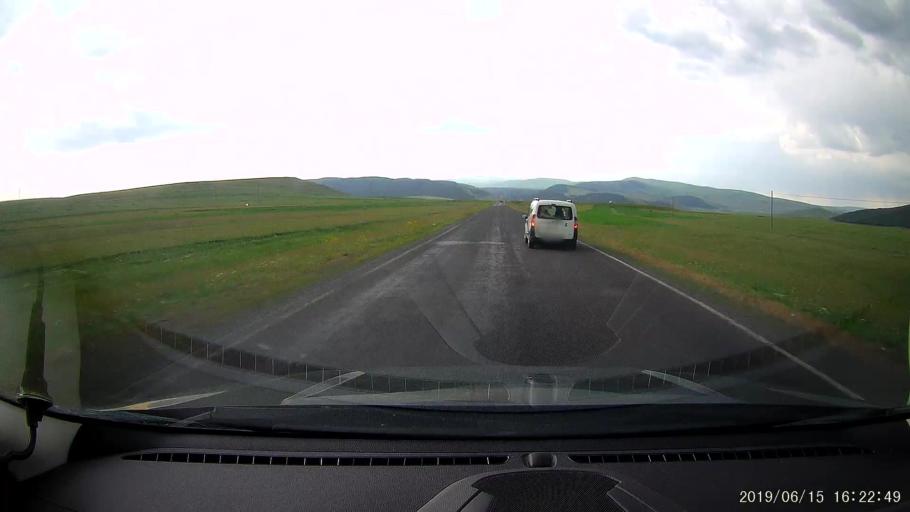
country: TR
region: Ardahan
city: Hanak
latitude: 41.1845
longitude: 42.8549
